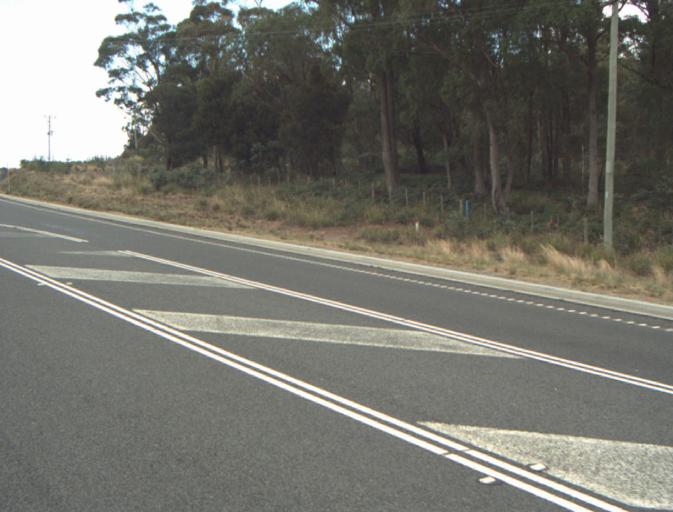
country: AU
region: Tasmania
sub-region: Launceston
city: Mayfield
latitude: -41.2653
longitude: 147.0326
